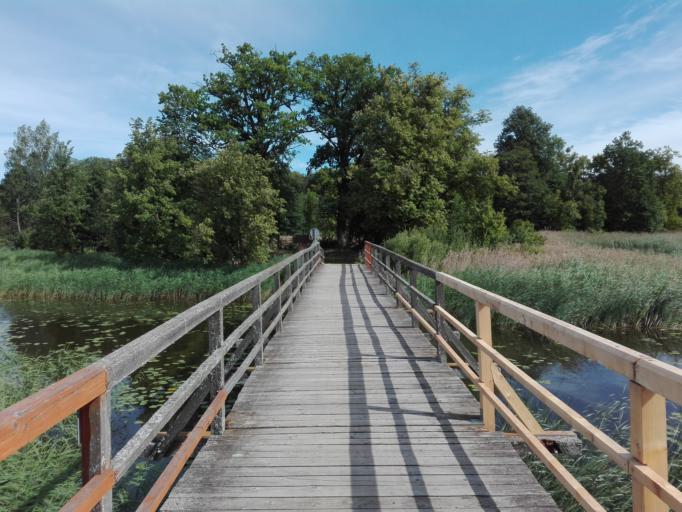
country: LT
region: Panevezys
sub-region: Birzai
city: Birzai
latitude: 56.2166
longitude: 24.7699
